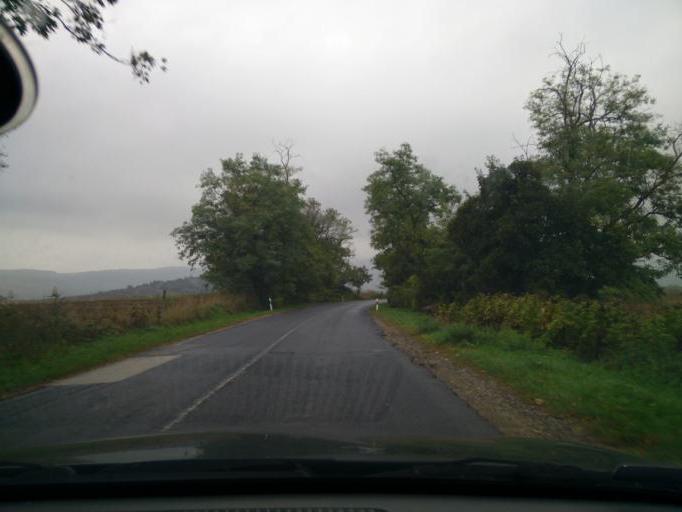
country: HU
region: Komarom-Esztergom
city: Tarjan
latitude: 47.6335
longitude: 18.5165
